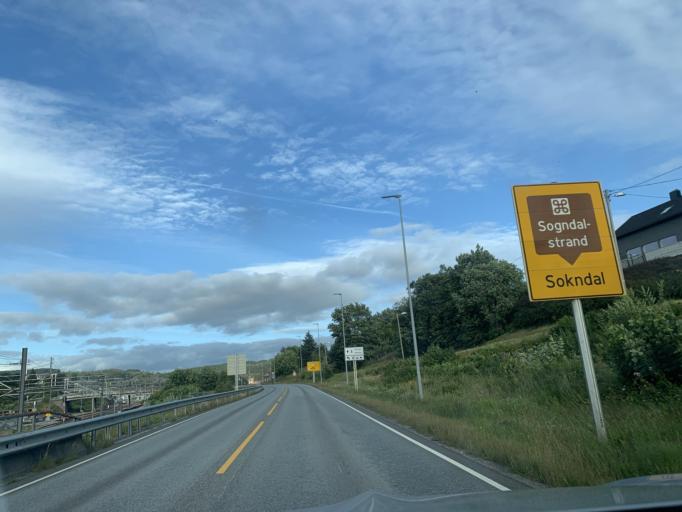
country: NO
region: Rogaland
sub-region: Eigersund
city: Egersund
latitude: 58.4613
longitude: 5.9961
